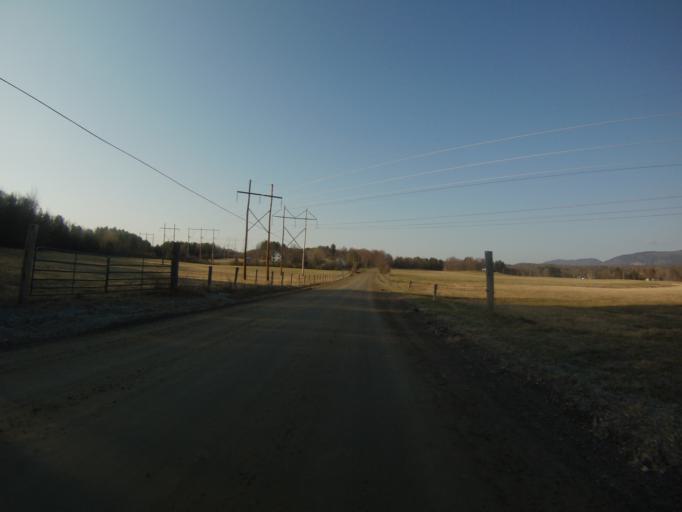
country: US
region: Vermont
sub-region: Addison County
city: Middlebury (village)
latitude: 44.0458
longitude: -73.1465
